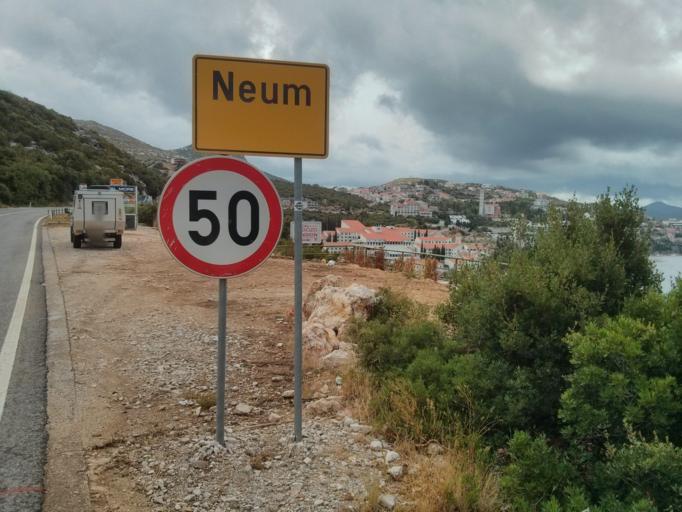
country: BA
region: Federation of Bosnia and Herzegovina
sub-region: Hercegovacko-Bosanski Kanton
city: Neum
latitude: 42.9294
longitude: 17.6028
